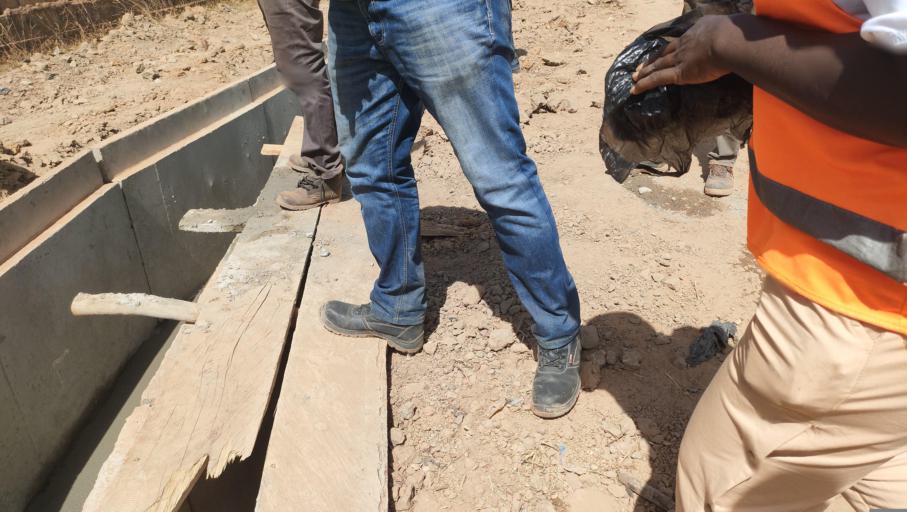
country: BF
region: Est
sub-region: Province du Gourma
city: Fada N'gourma
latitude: 12.0741
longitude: 0.3270
